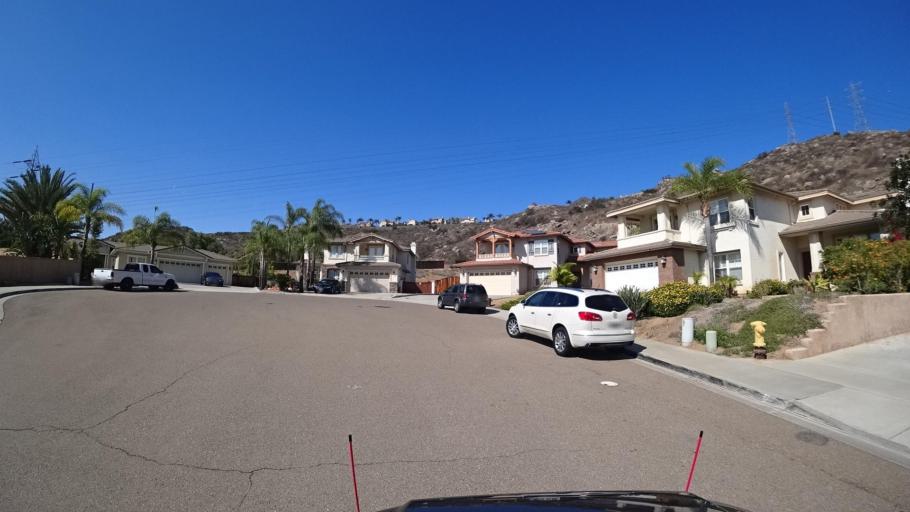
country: US
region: California
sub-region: San Diego County
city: Rancho San Diego
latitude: 32.7607
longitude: -116.9006
